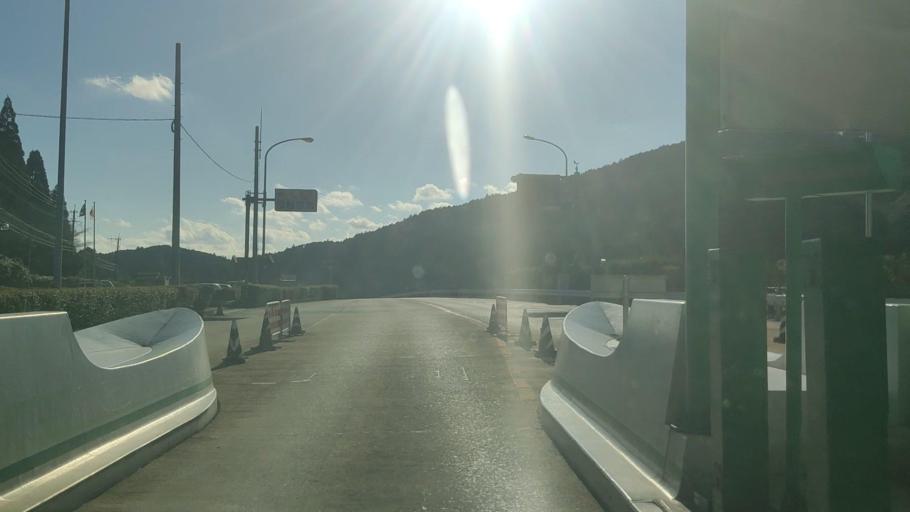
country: JP
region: Fukuoka
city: Maebaru-chuo
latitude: 33.4632
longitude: 130.2756
